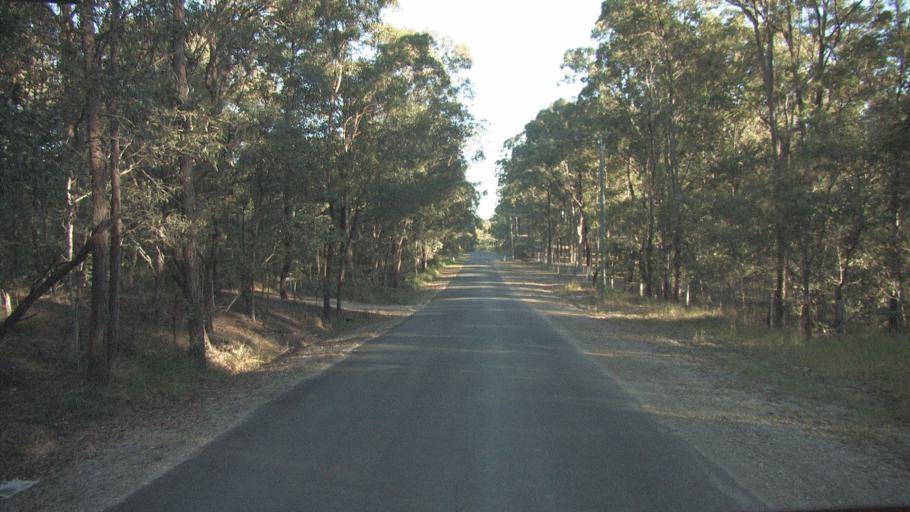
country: AU
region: Queensland
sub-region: Logan
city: Chambers Flat
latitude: -27.7646
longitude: 153.1281
